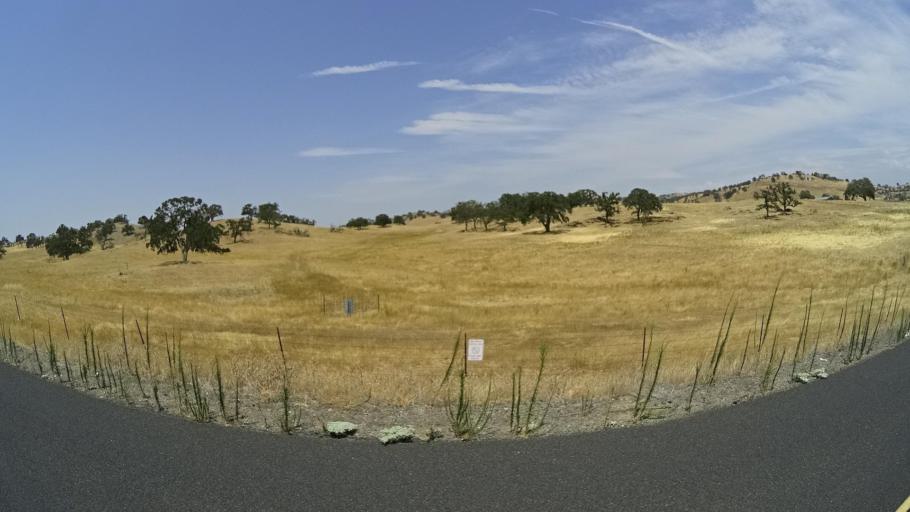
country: US
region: California
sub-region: Tuolumne County
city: Jamestown
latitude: 37.6301
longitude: -120.3630
